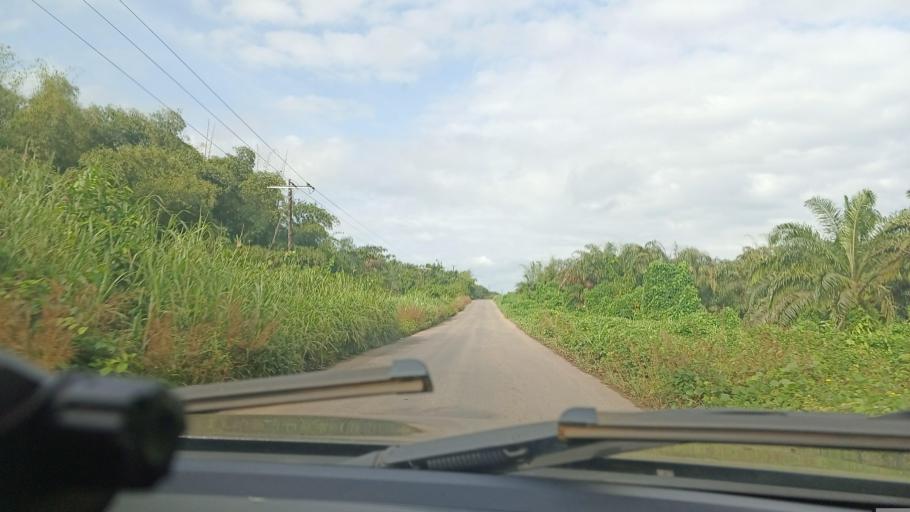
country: LR
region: Bomi
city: Tubmanburg
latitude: 6.7124
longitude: -10.9461
